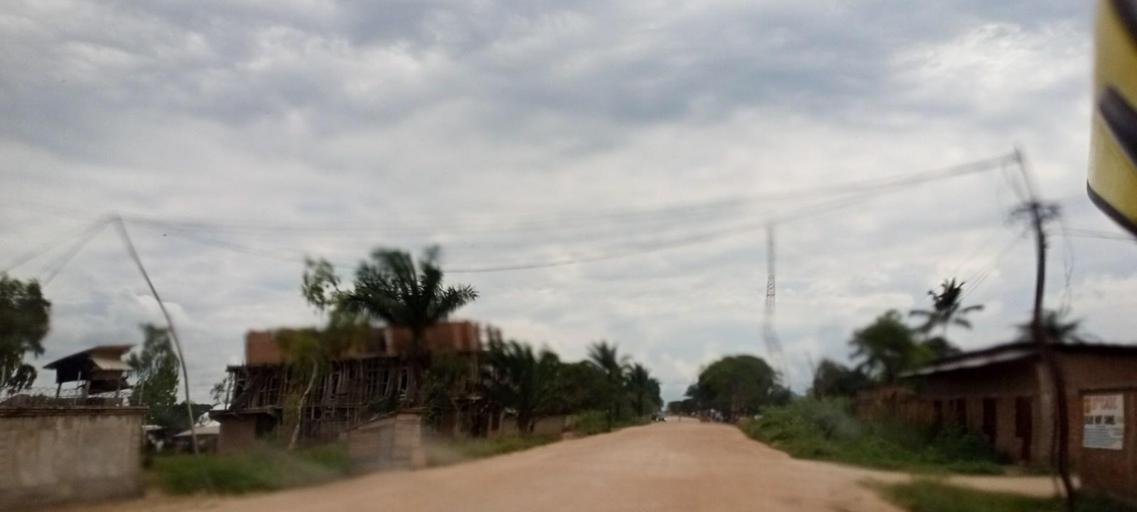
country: CD
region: South Kivu
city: Uvira
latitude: -3.3423
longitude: 29.1936
